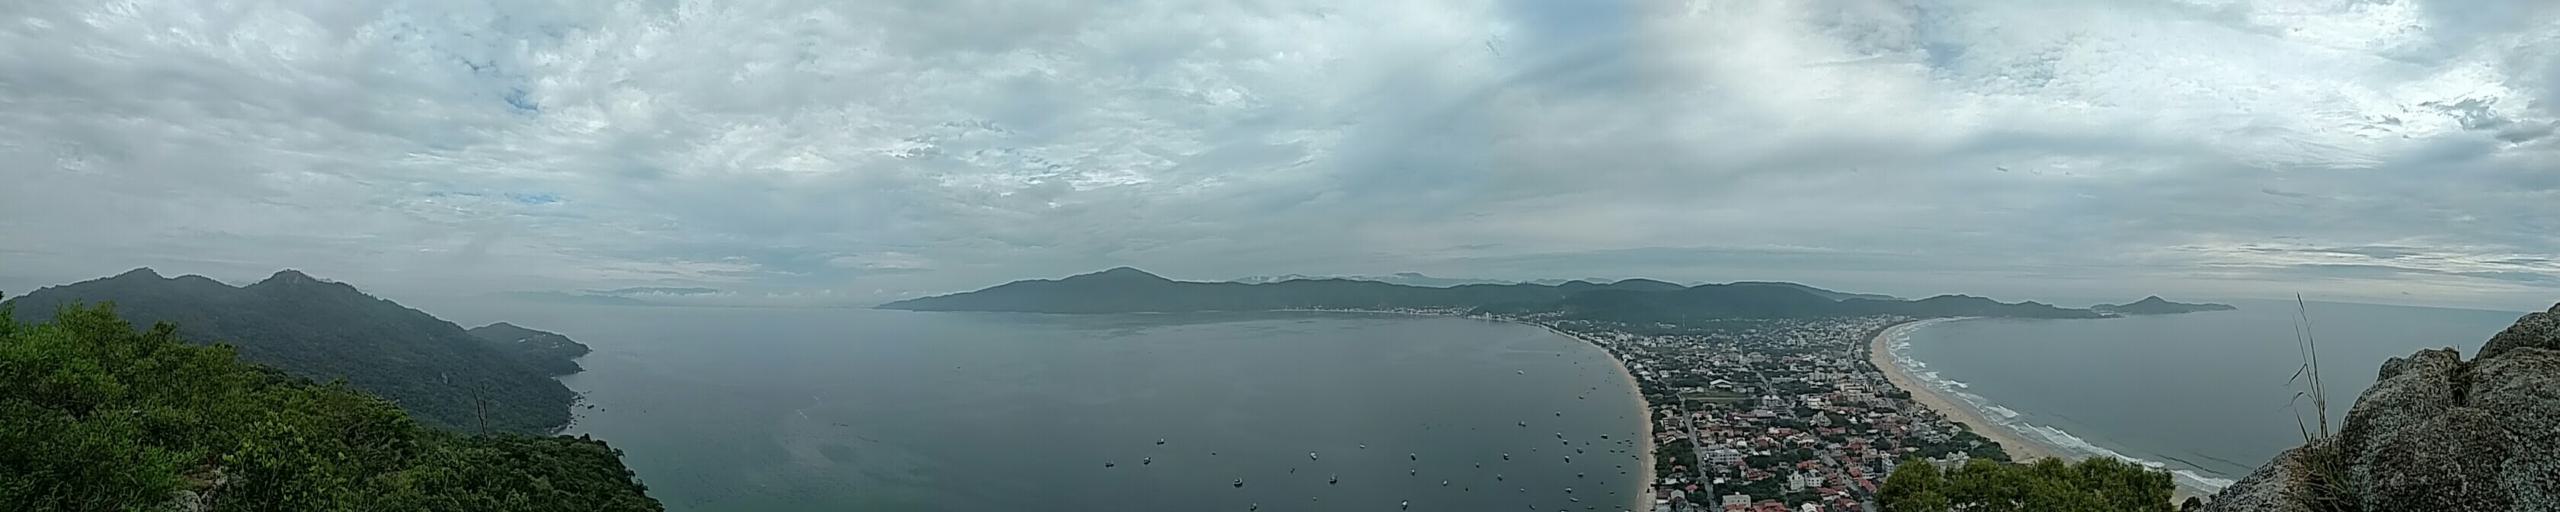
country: BR
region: Santa Catarina
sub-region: Porto Belo
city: Porto Belo
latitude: -27.2031
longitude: -48.4967
